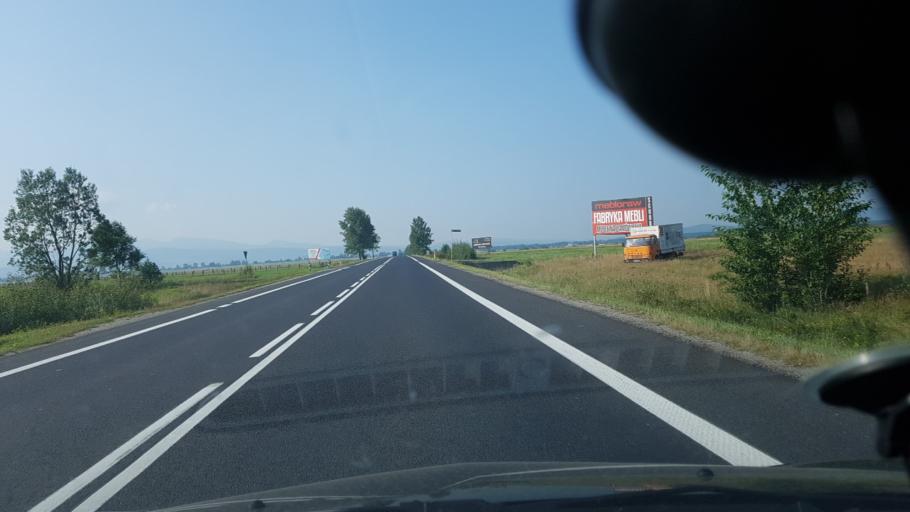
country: PL
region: Lesser Poland Voivodeship
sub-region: Powiat nowotarski
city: Chyzne
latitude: 49.4497
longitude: 19.6863
